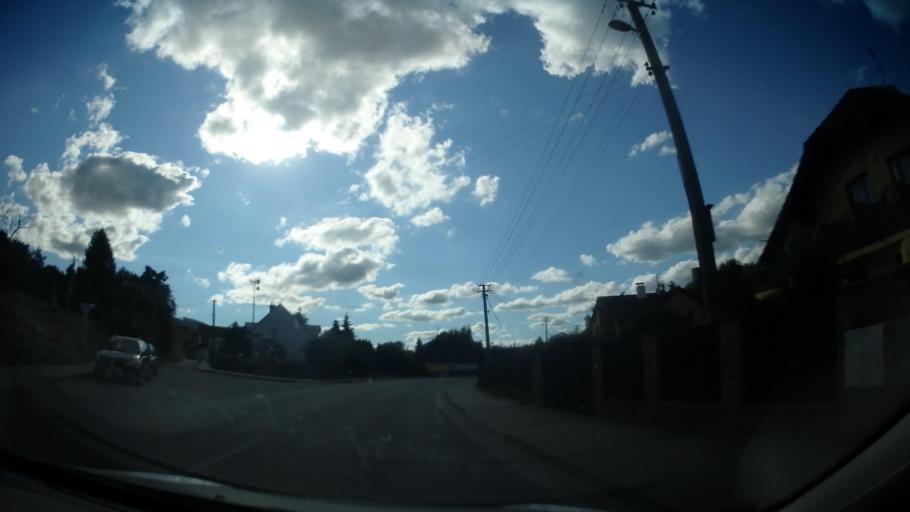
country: CZ
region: South Moravian
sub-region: Okres Blansko
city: Rajec-Jestrebi
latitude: 49.4099
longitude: 16.6201
